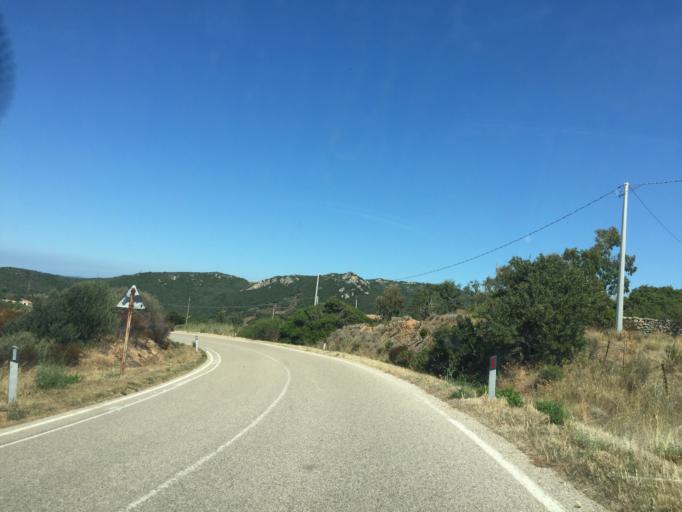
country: IT
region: Sardinia
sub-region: Provincia di Olbia-Tempio
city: Aglientu
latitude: 41.0952
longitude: 9.0995
